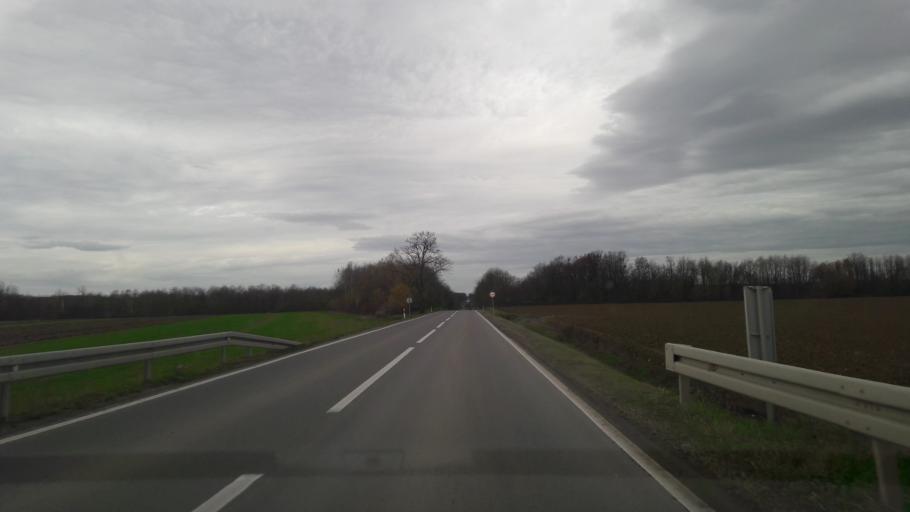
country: HR
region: Osjecko-Baranjska
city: Fericanci
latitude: 45.5345
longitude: 17.9398
